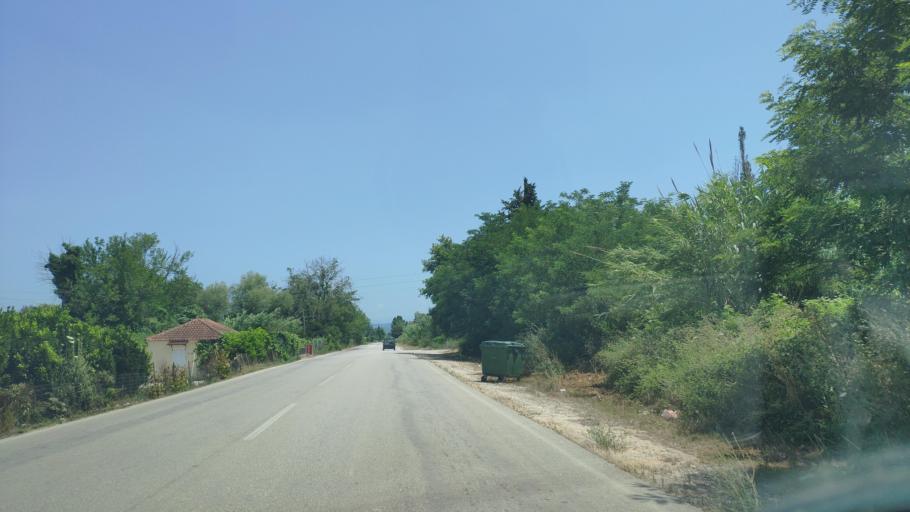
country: GR
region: Epirus
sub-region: Nomos Artas
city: Aneza
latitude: 39.1082
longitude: 20.9211
